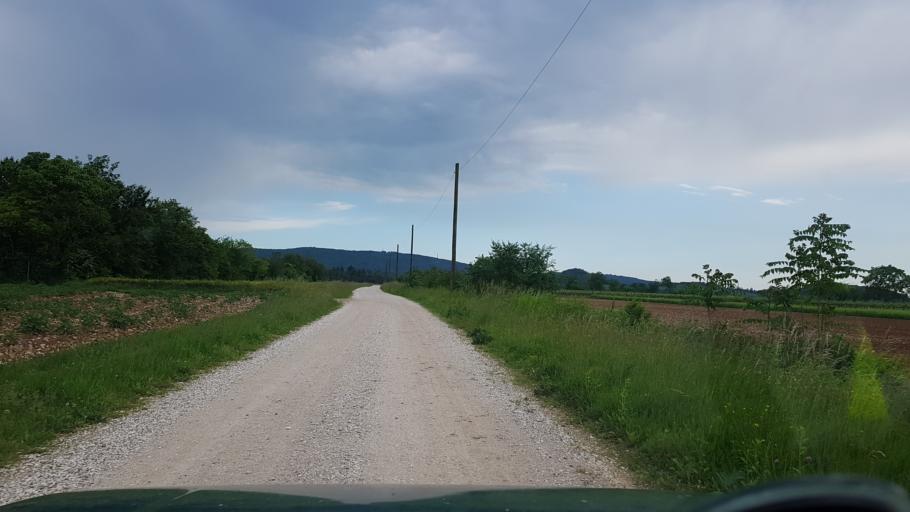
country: IT
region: Friuli Venezia Giulia
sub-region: Provincia di Gorizia
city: Mossa
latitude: 45.9289
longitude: 13.5426
